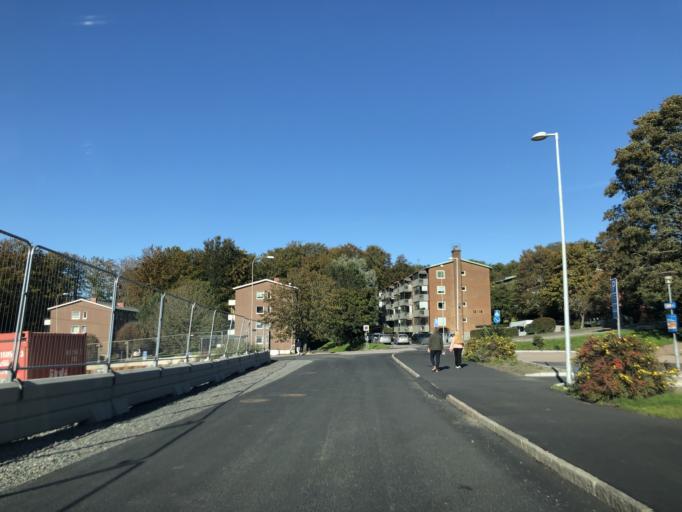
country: SE
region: Vaestra Goetaland
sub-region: Molndal
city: Moelndal
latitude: 57.6795
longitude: 12.0141
